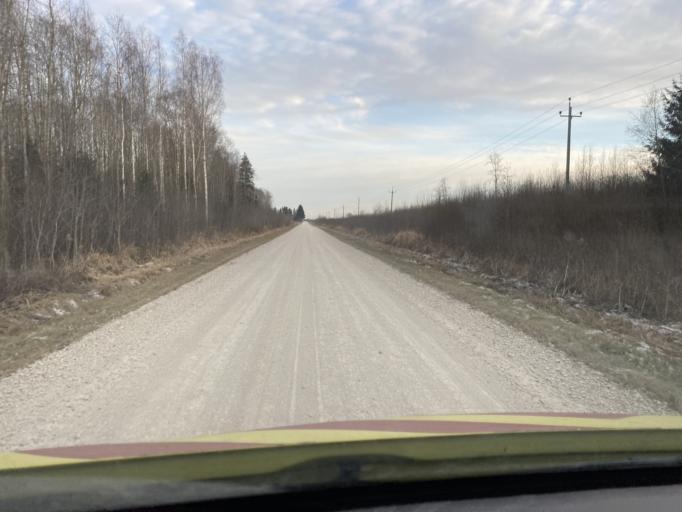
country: EE
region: Jogevamaa
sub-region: Poltsamaa linn
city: Poltsamaa
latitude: 58.5829
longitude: 26.0559
